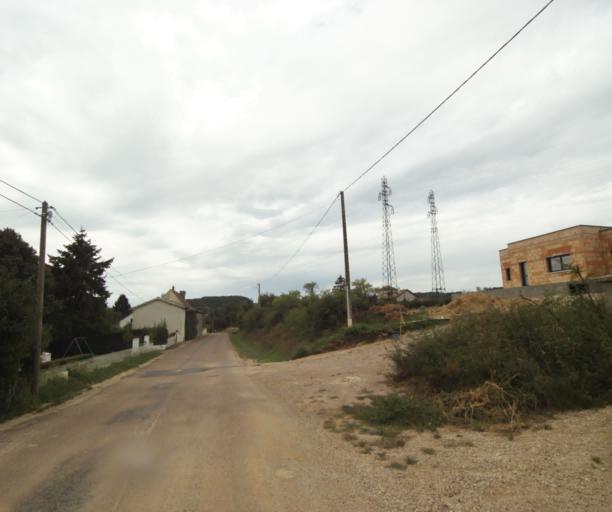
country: FR
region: Bourgogne
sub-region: Departement de Saone-et-Loire
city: Tournus
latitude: 46.5655
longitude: 4.8890
